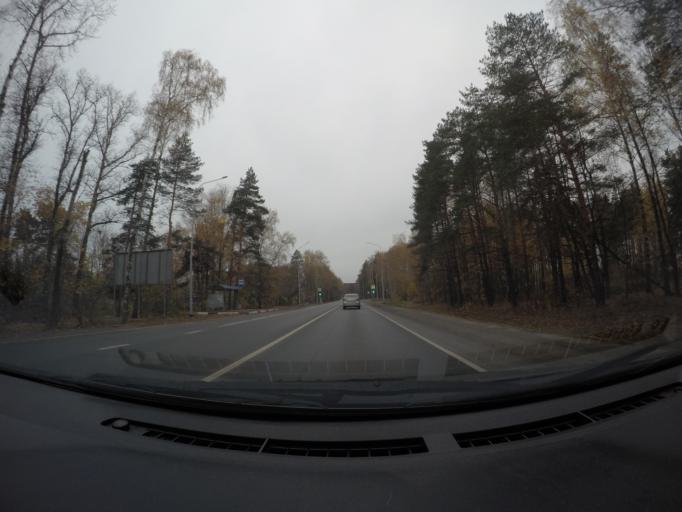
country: RU
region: Moskovskaya
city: Malyshevo
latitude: 55.4905
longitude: 38.3653
